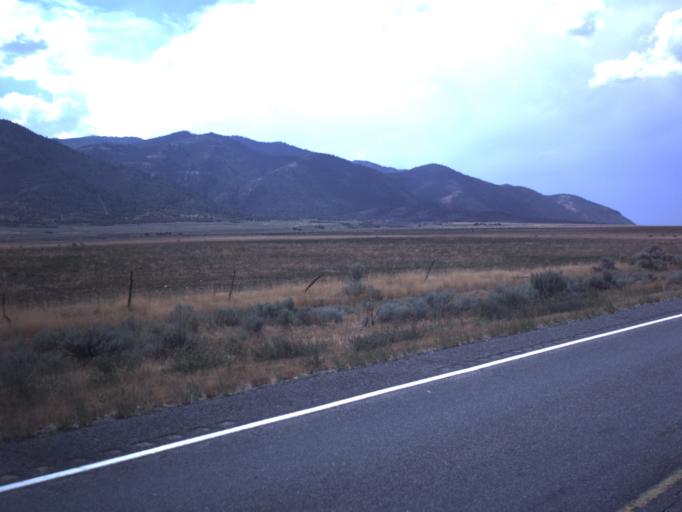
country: US
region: Utah
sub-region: Sanpete County
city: Fountain Green
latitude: 39.6522
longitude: -111.6490
